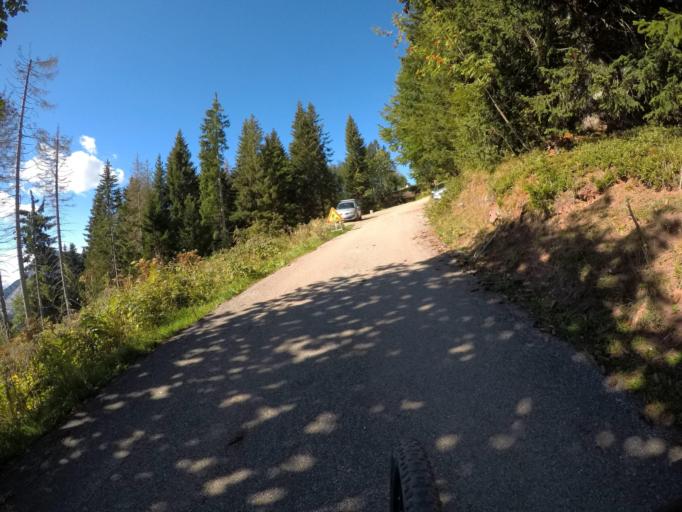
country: IT
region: Friuli Venezia Giulia
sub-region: Provincia di Udine
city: Ligosullo
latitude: 46.5505
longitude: 13.0929
